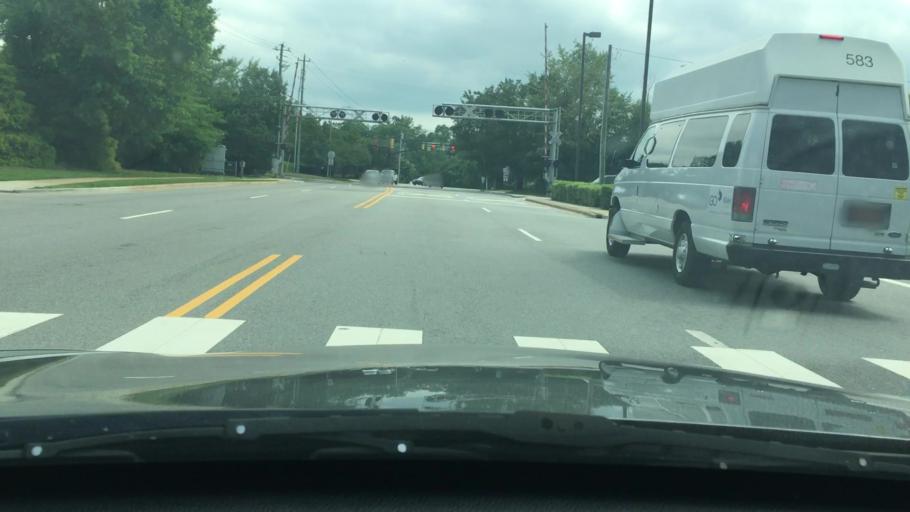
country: US
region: North Carolina
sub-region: Wake County
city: Cary
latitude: 35.7885
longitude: -78.7833
